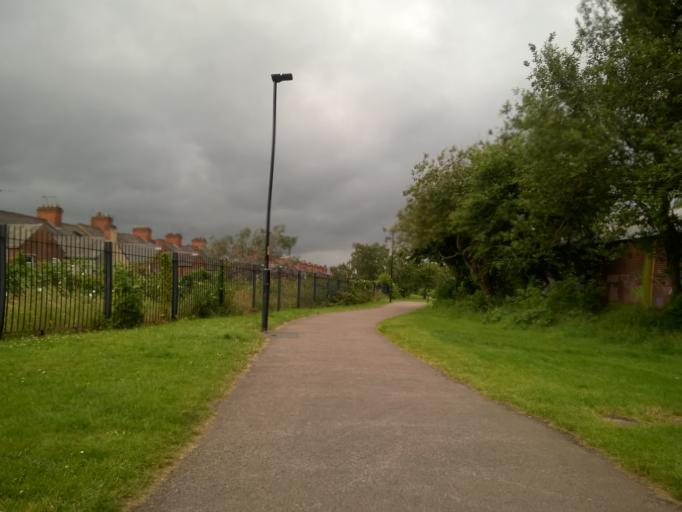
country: GB
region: England
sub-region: City of Leicester
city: Leicester
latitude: 52.6398
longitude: -1.1491
